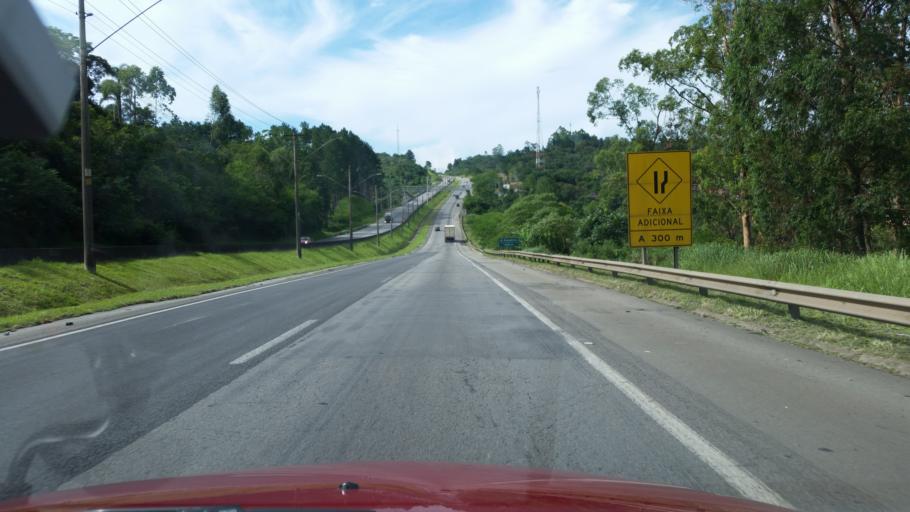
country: BR
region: Sao Paulo
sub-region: Sao Lourenco Da Serra
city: Sao Lourenco da Serra
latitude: -23.8149
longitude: -46.9237
